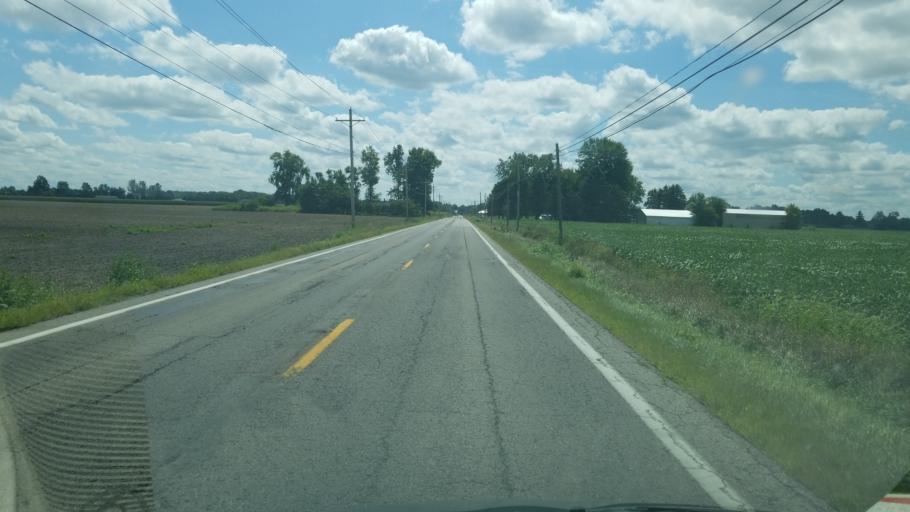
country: US
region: Ohio
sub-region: Henry County
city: Liberty Center
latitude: 41.4647
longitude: -84.0088
